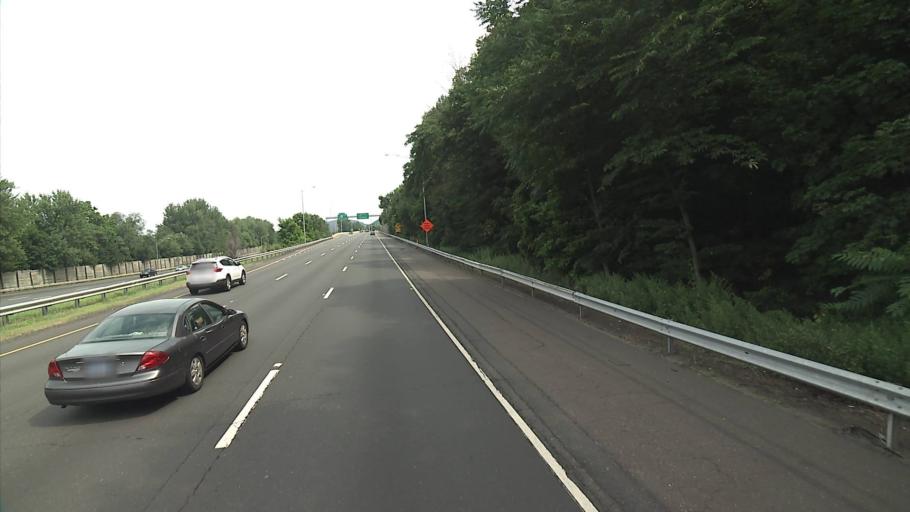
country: US
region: Connecticut
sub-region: Hartford County
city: Plainville
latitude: 41.6637
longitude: -72.8470
